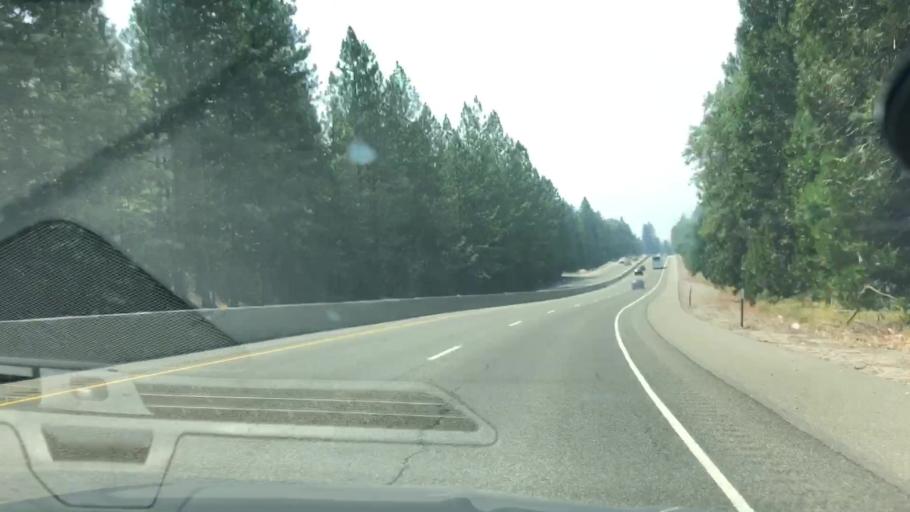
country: US
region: California
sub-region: El Dorado County
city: Camino
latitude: 38.7344
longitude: -120.6710
